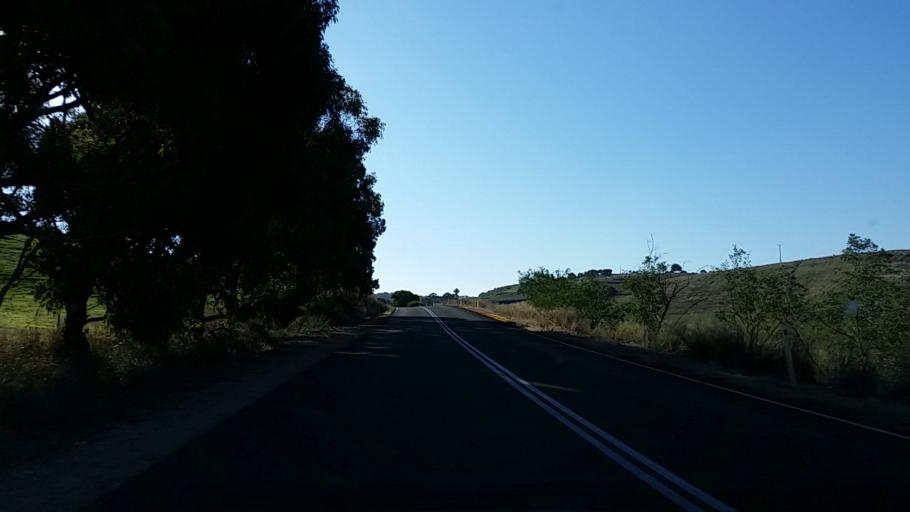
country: AU
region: South Australia
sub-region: Alexandrina
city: Strathalbyn
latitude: -35.1836
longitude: 138.9488
